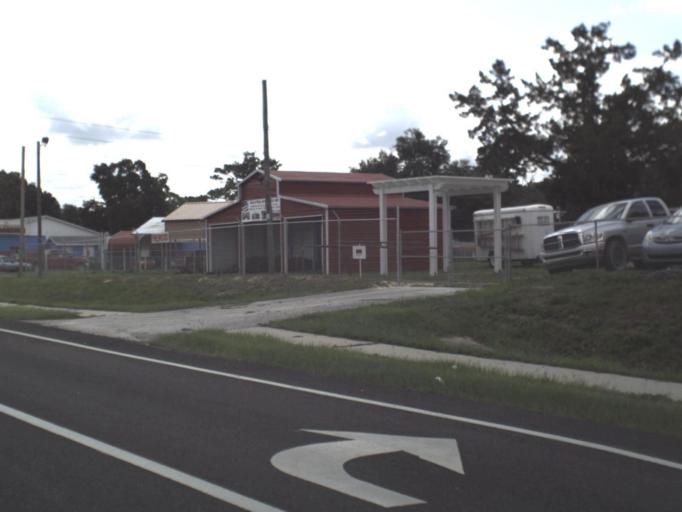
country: US
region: Florida
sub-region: Hernando County
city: Brookridge
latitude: 28.5408
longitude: -82.4595
